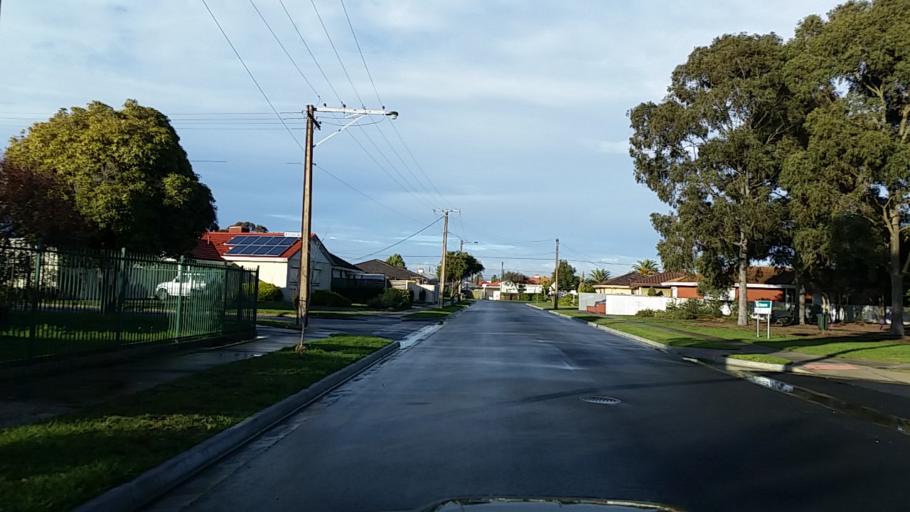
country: AU
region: South Australia
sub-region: Charles Sturt
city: Findon
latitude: -34.8995
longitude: 138.5353
